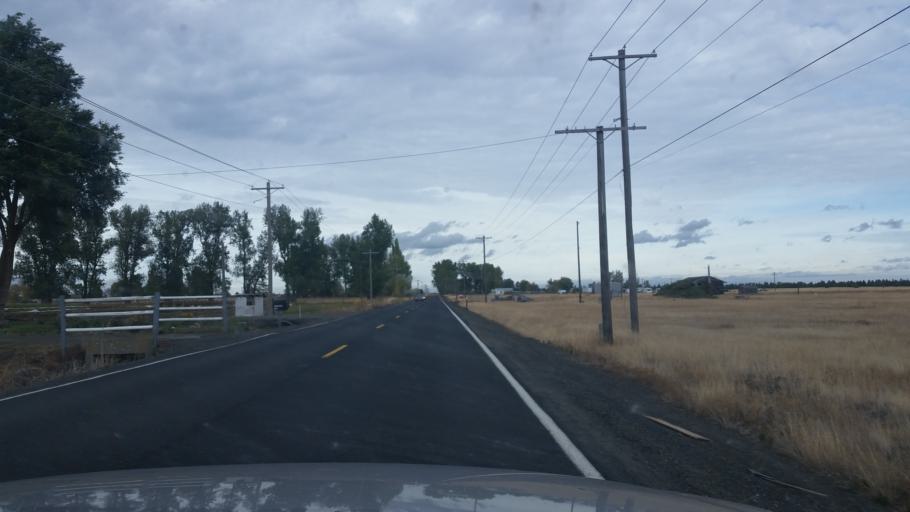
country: US
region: Washington
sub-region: Spokane County
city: Airway Heights
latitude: 47.6071
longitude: -117.6075
